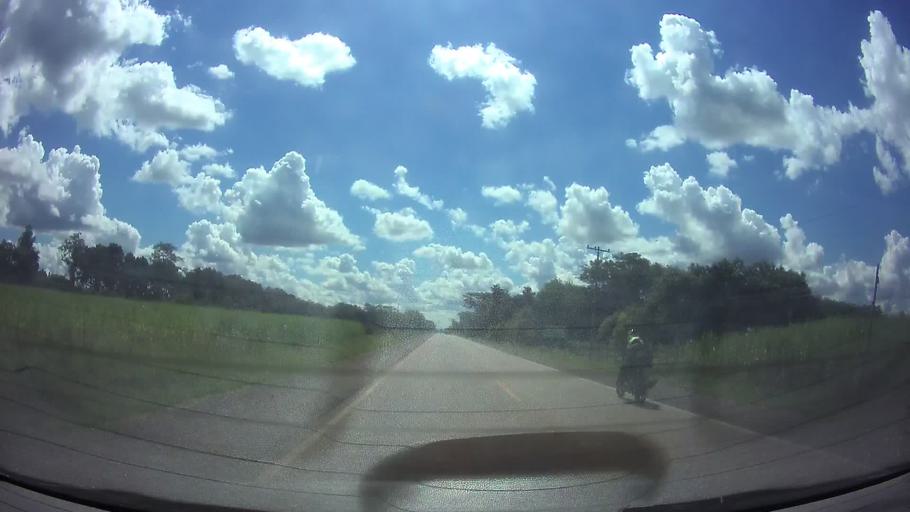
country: PY
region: Paraguari
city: La Colmena
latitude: -25.9053
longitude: -56.7678
